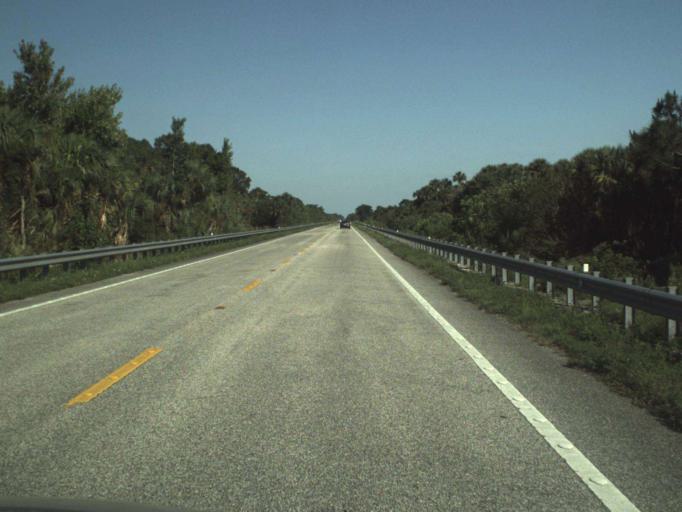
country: US
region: Florida
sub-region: Seminole County
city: Geneva
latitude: 28.7077
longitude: -81.0191
